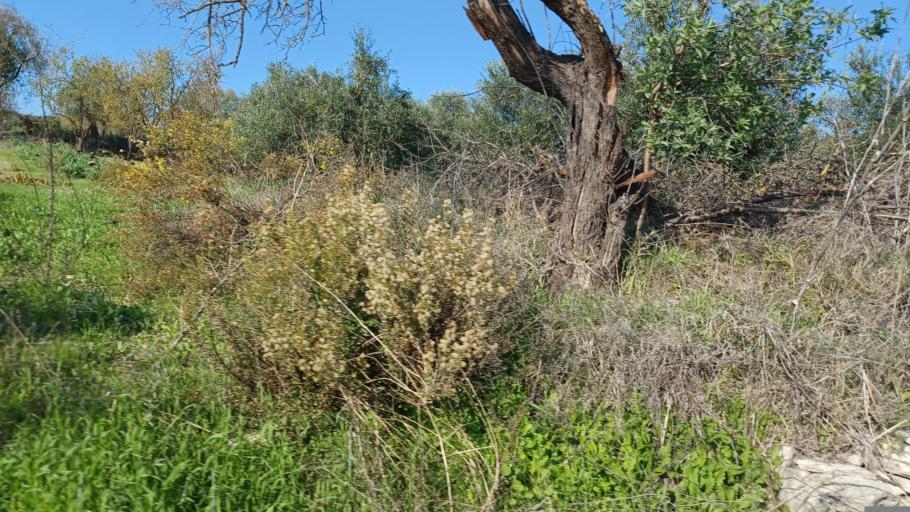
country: CY
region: Pafos
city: Mesogi
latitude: 34.8560
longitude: 32.5108
